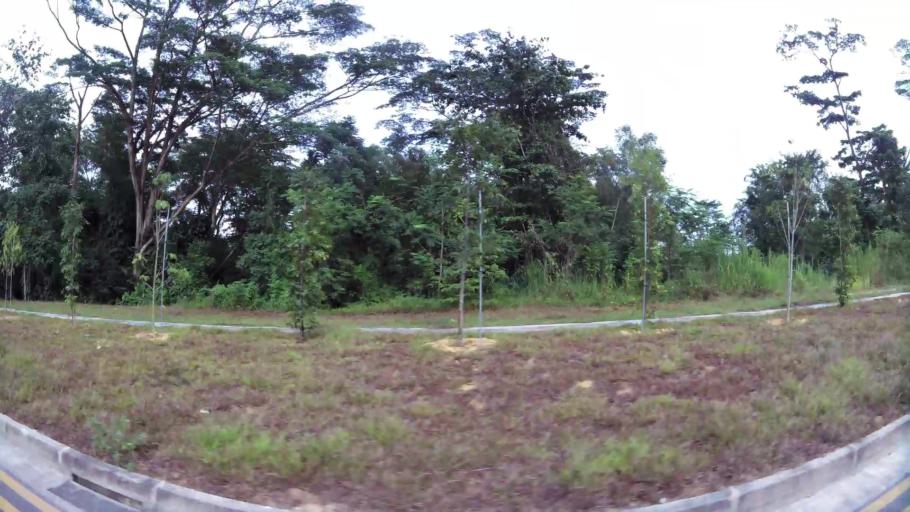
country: MY
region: Johor
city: Johor Bahru
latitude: 1.3611
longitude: 103.6936
